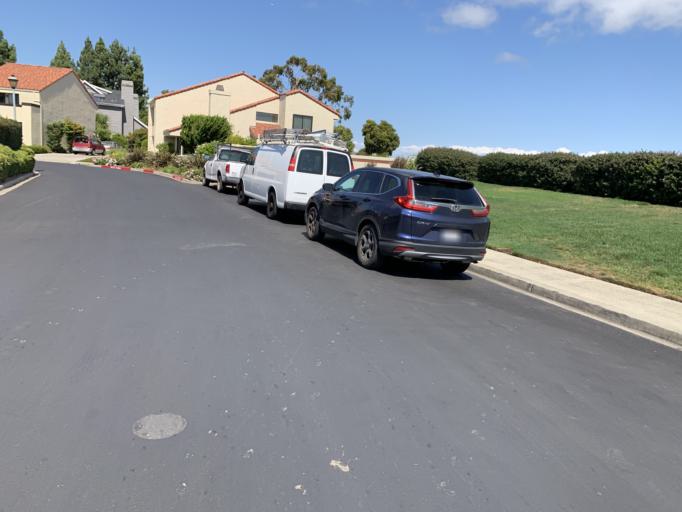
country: US
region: California
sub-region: San Mateo County
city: Redwood Shores
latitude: 37.5317
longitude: -122.2419
